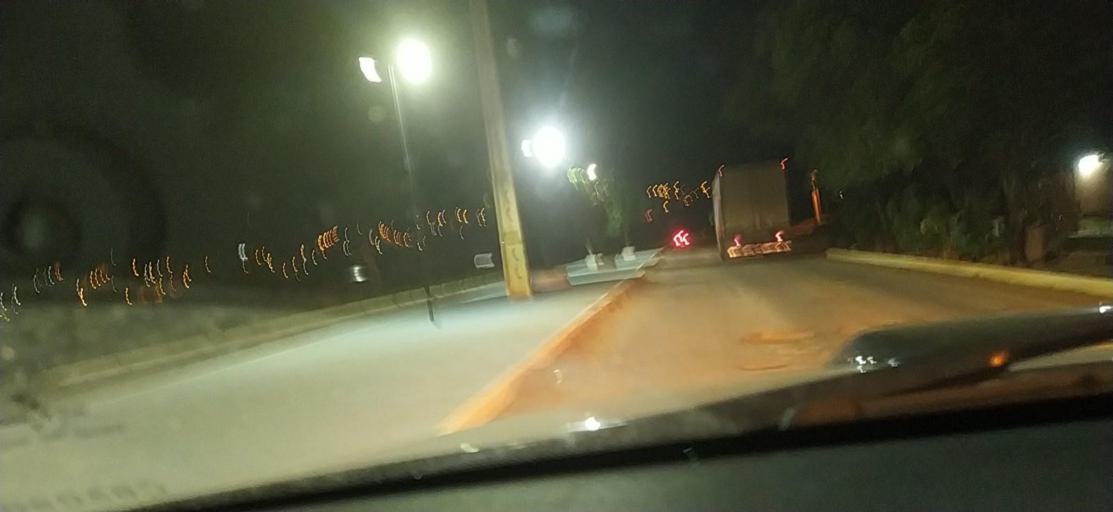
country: BR
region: Minas Gerais
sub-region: Monte Azul
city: Monte Azul
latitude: -15.1584
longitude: -42.8661
